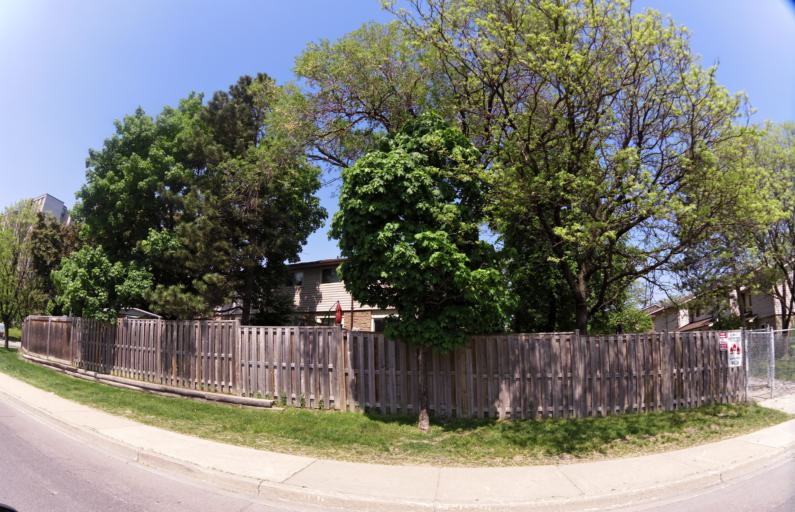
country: CA
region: Ontario
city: Mississauga
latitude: 43.6061
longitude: -79.6338
